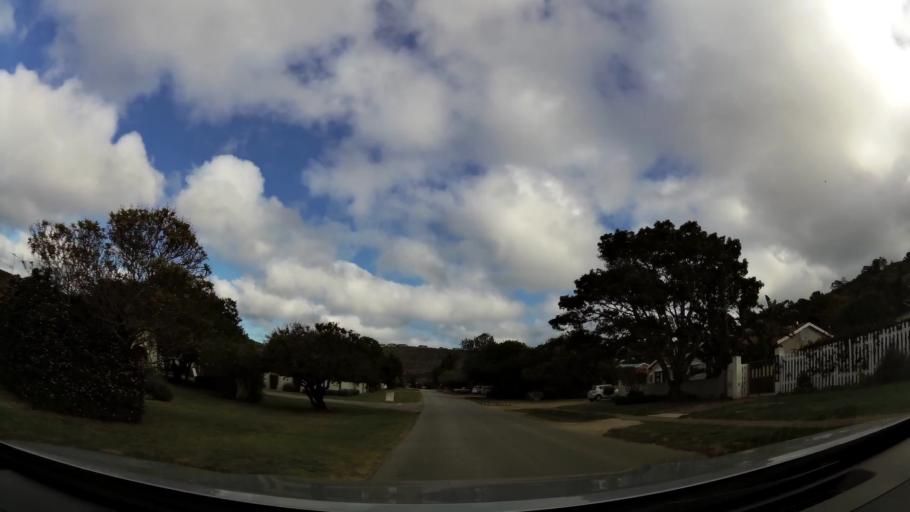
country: ZA
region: Western Cape
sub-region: Eden District Municipality
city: Plettenberg Bay
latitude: -34.0799
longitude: 23.3637
